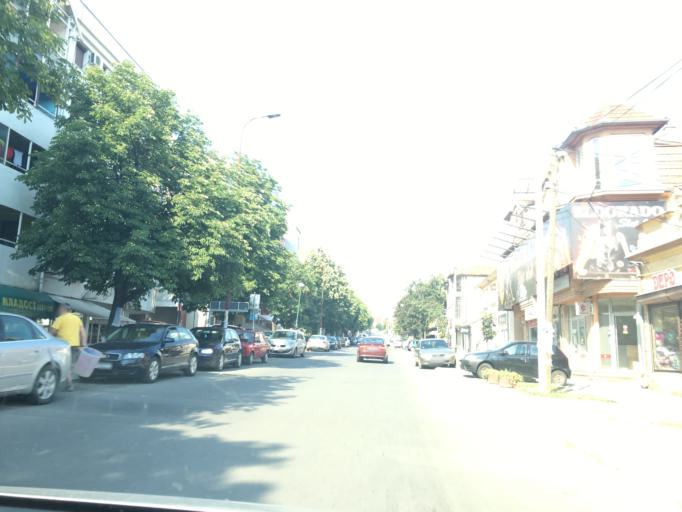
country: RS
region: Central Serbia
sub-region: Belgrade
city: Lazarevac
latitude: 44.3801
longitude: 20.2657
